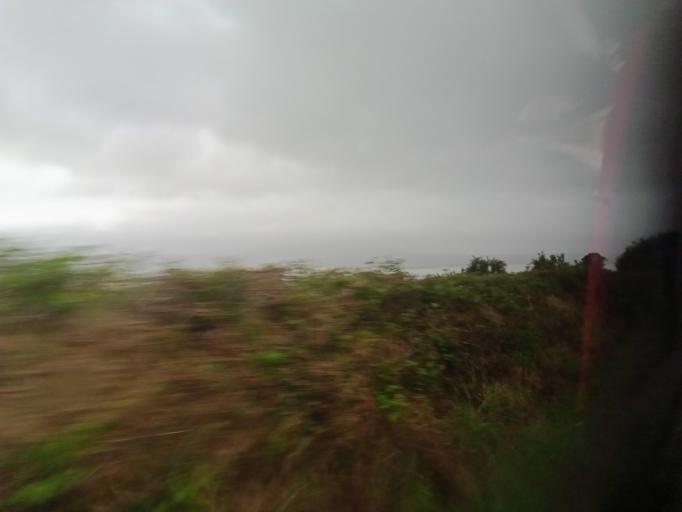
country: IE
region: Munster
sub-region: Waterford
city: Dungarvan
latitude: 52.0497
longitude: -7.6420
